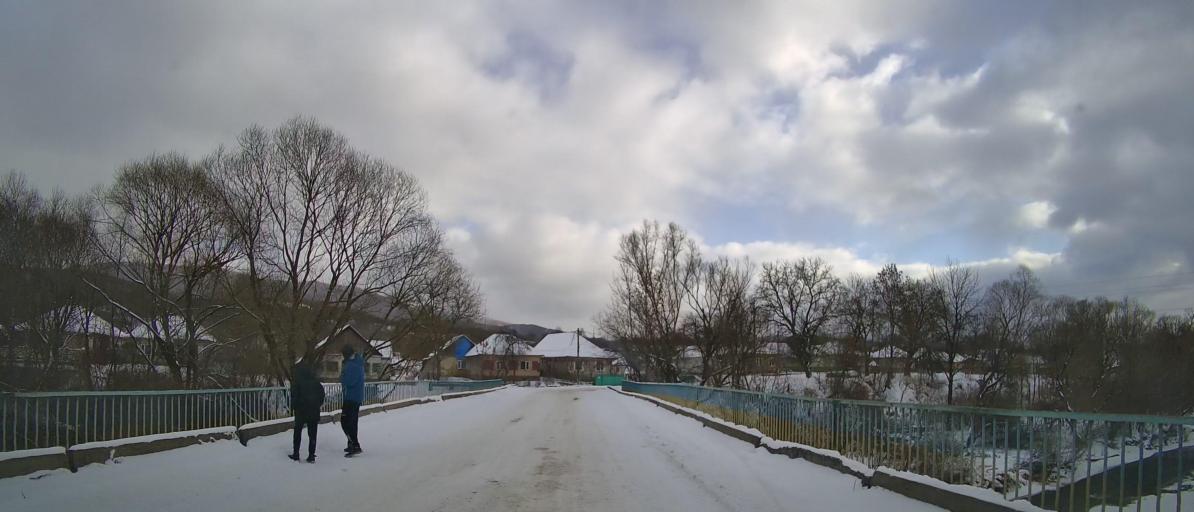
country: UA
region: Zakarpattia
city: Velykyi Bereznyi
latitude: 48.9218
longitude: 22.4630
